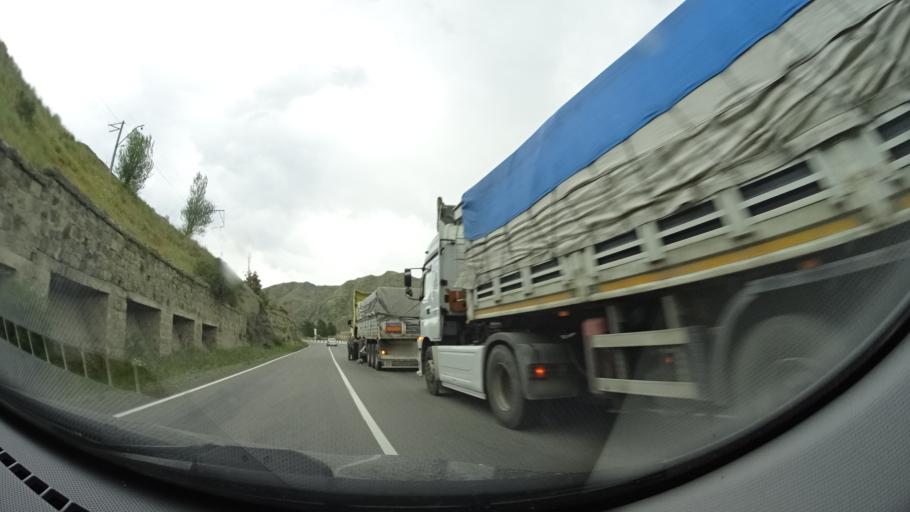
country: GE
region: Samtskhe-Javakheti
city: Akhaltsikhe
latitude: 41.6785
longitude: 43.0716
